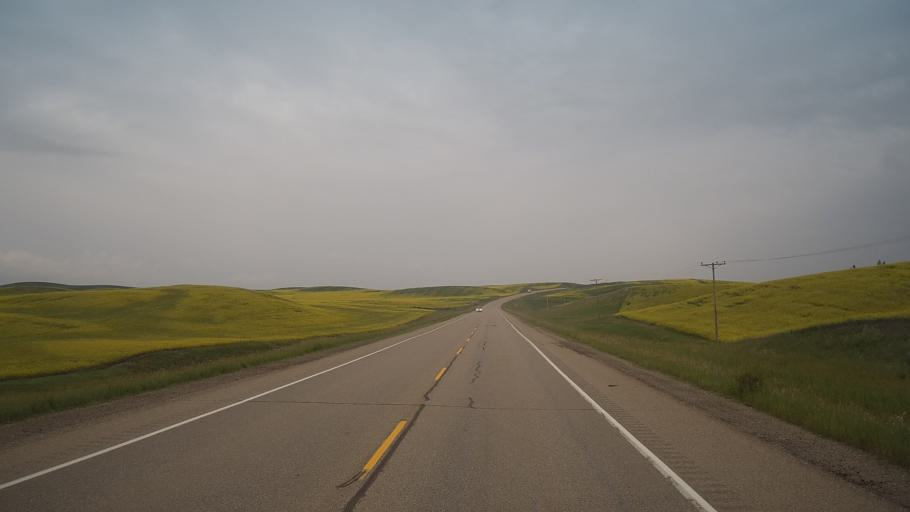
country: CA
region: Saskatchewan
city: Biggar
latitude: 52.0548
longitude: -107.7538
